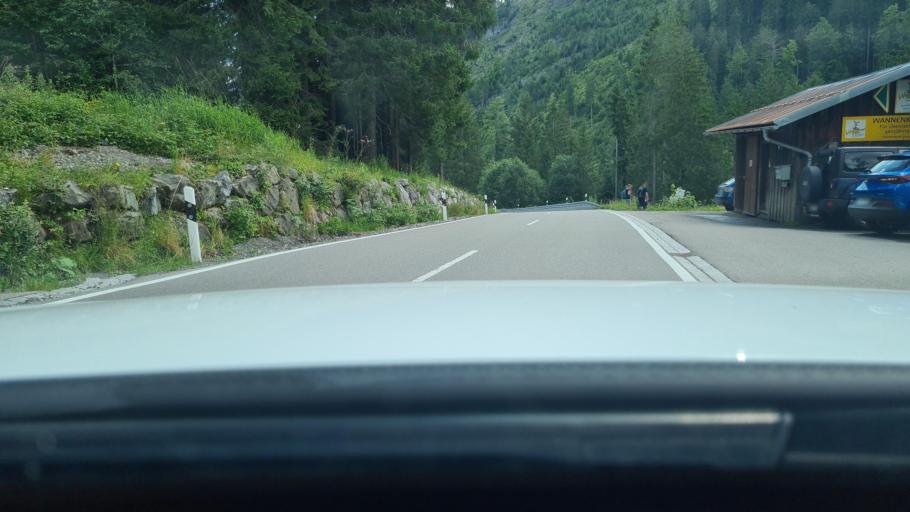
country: DE
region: Bavaria
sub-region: Swabia
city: Obermaiselstein
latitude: 47.4340
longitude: 10.2002
